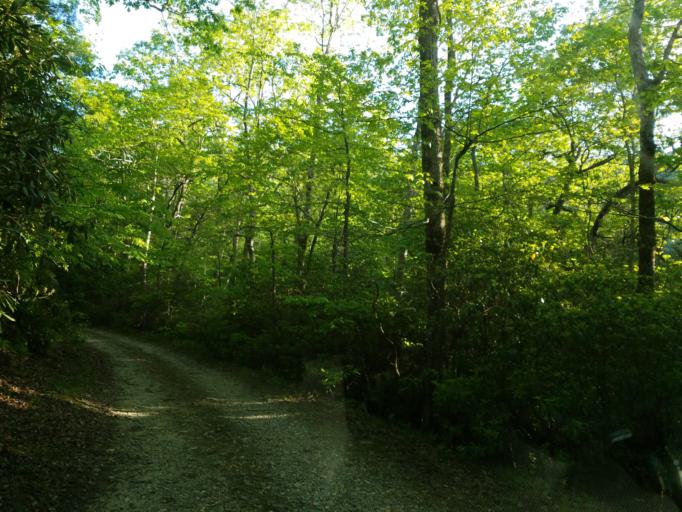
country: US
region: Georgia
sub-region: Lumpkin County
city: Dahlonega
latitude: 34.6692
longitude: -84.1299
